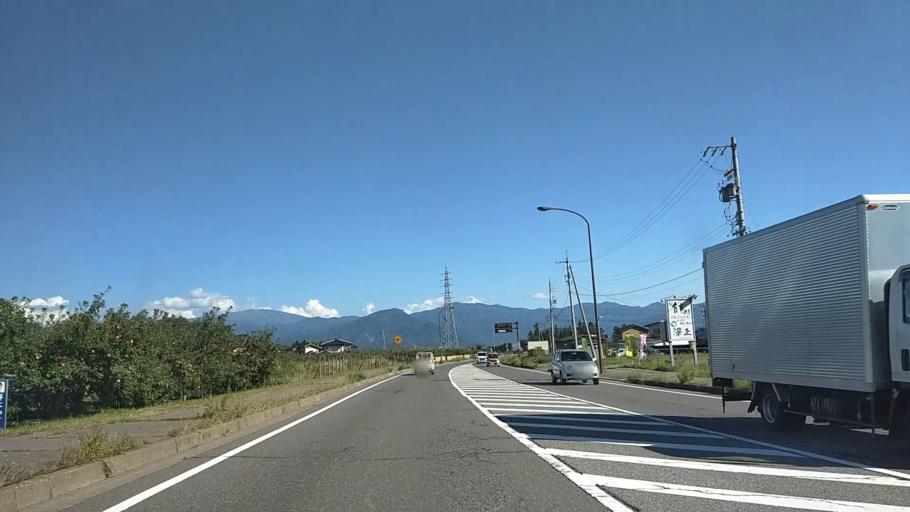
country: JP
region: Nagano
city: Nagano-shi
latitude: 36.6161
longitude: 138.1359
